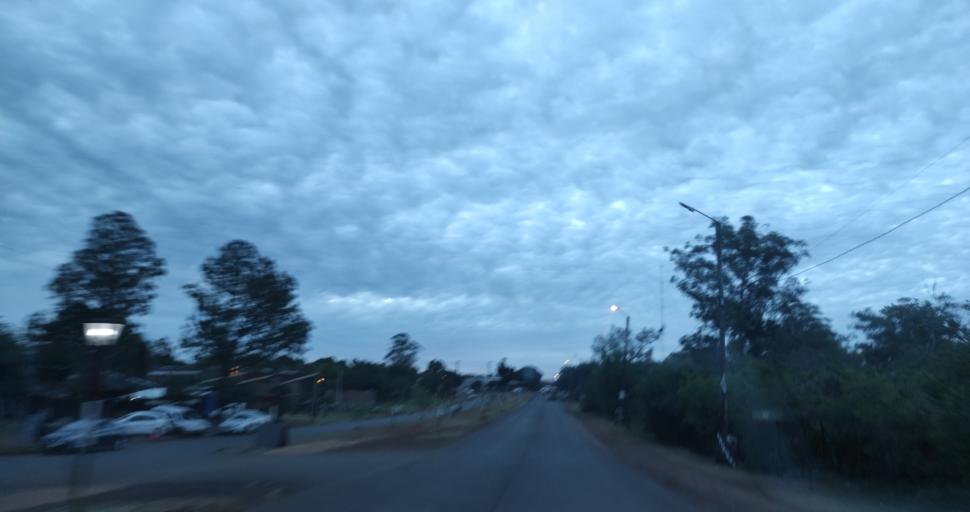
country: AR
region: Misiones
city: Garupa
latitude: -27.4669
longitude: -55.8530
